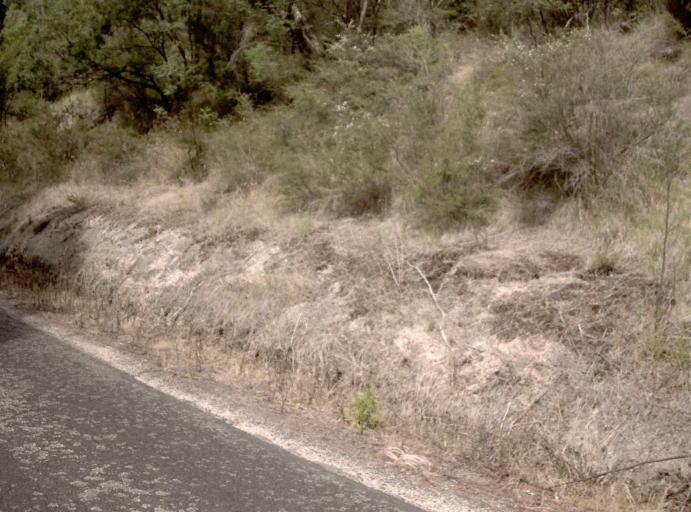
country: AU
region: New South Wales
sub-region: Bega Valley
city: Eden
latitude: -37.4812
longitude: 149.6059
